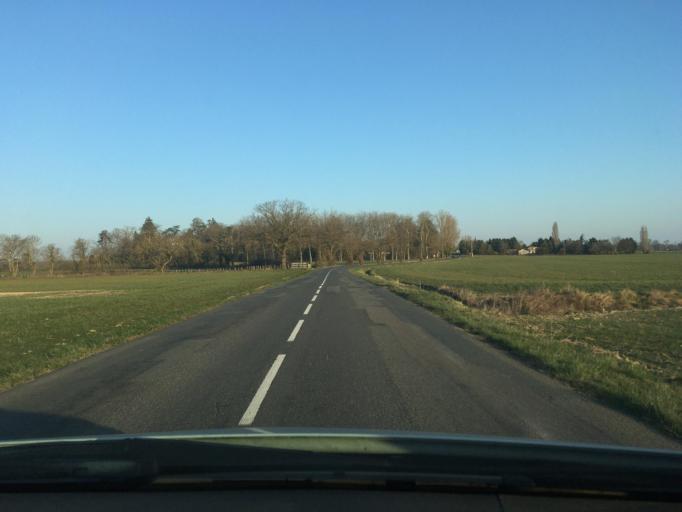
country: FR
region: Rhone-Alpes
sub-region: Departement de l'Ain
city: Saint-Andre-de-Corcy
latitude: 45.9373
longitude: 4.9445
